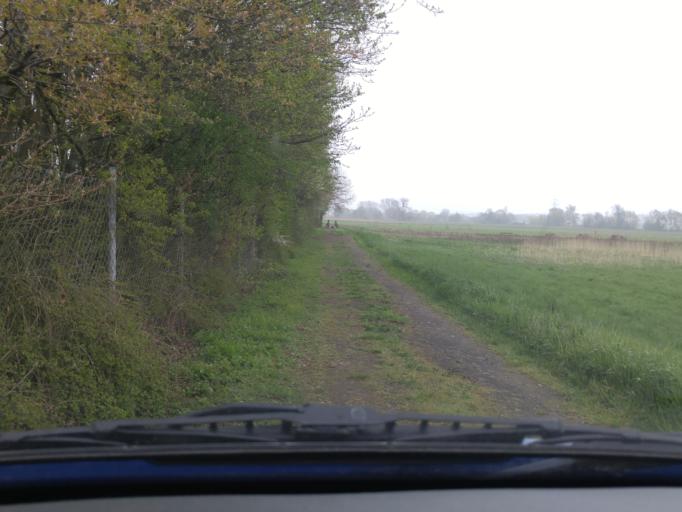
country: DE
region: Hesse
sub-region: Regierungsbezirk Darmstadt
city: Karben
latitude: 50.2750
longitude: 8.7768
